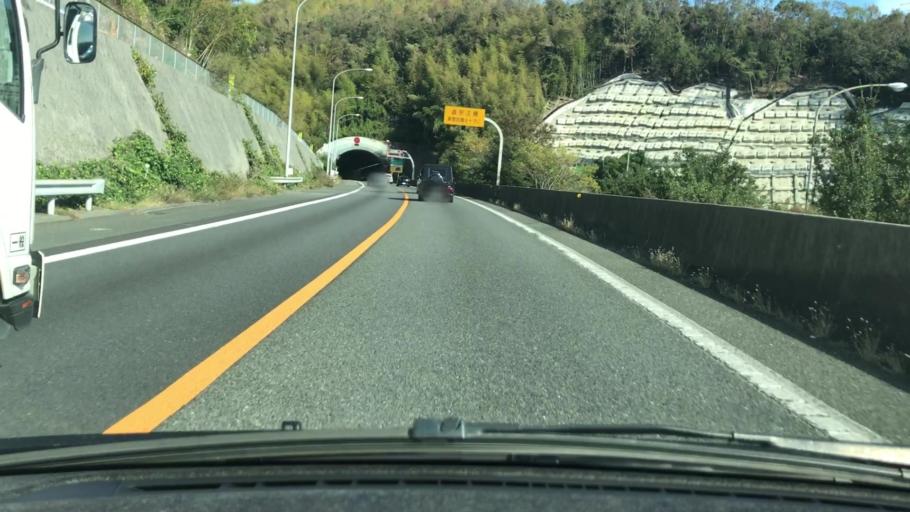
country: JP
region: Osaka
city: Takatsuki
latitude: 34.8674
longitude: 135.6488
